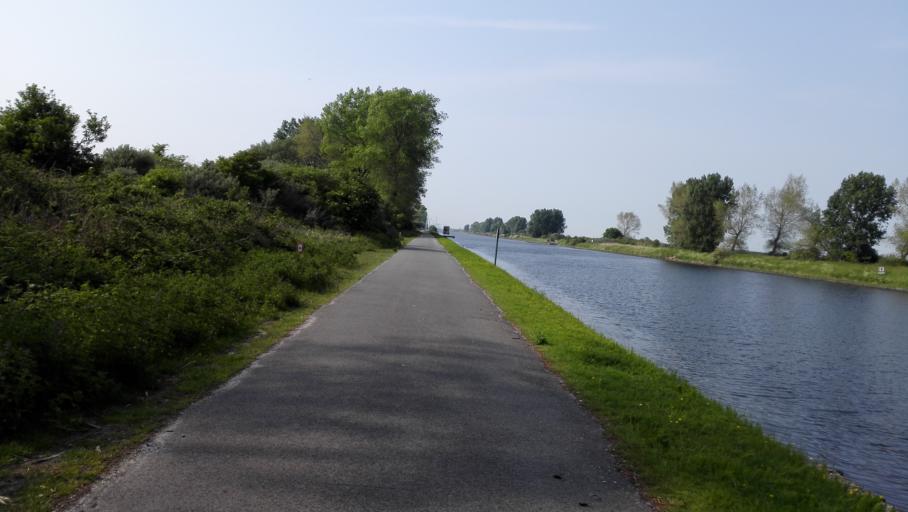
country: BE
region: Flanders
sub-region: Provincie West-Vlaanderen
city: Zeebrugge
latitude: 51.2902
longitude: 3.2072
